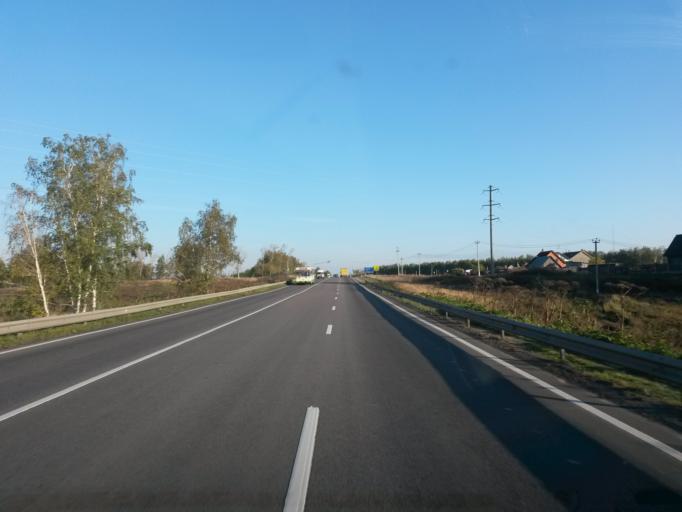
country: RU
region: Moskovskaya
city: Barybino
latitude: 55.2699
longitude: 37.8277
